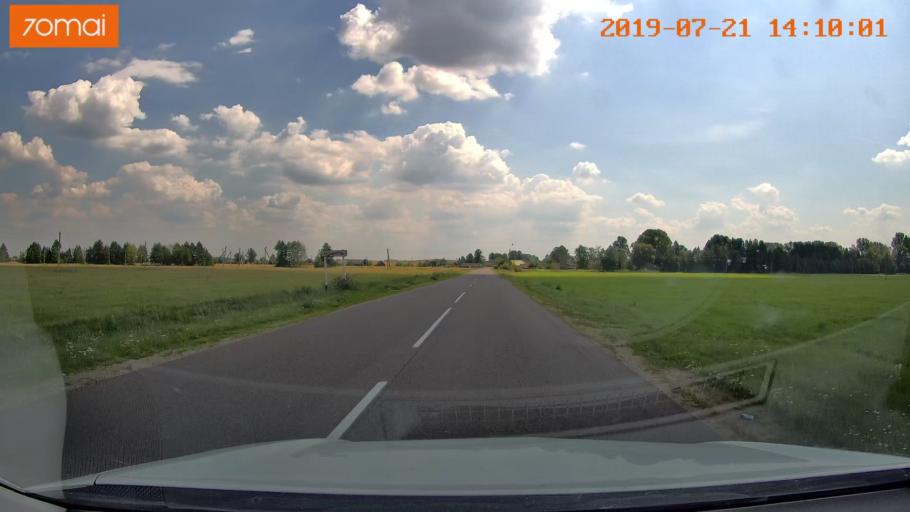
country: BY
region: Grodnenskaya
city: Karelichy
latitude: 53.6669
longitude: 26.1329
